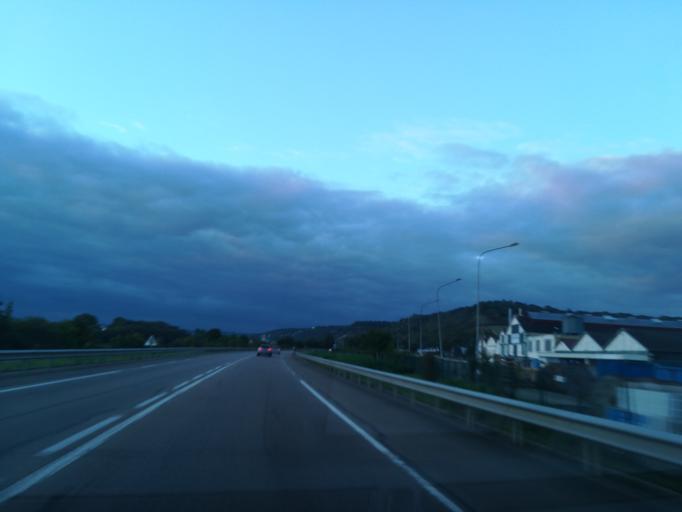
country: FR
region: Haute-Normandie
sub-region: Departement de la Seine-Maritime
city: Belbeuf
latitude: 49.3929
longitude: 1.1235
